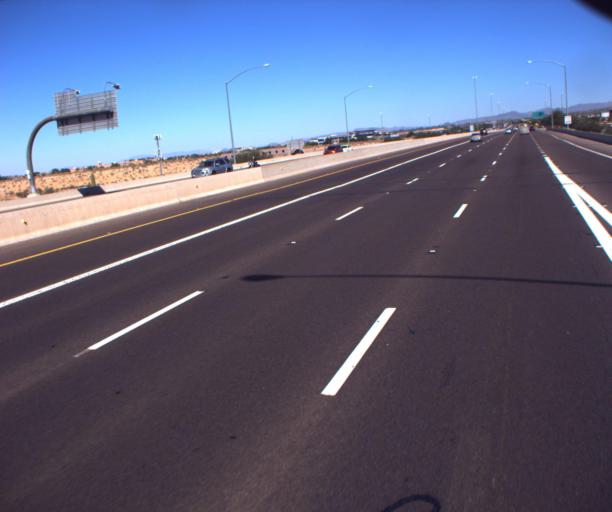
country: US
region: Arizona
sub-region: Maricopa County
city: Paradise Valley
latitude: 33.6298
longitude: -111.8902
